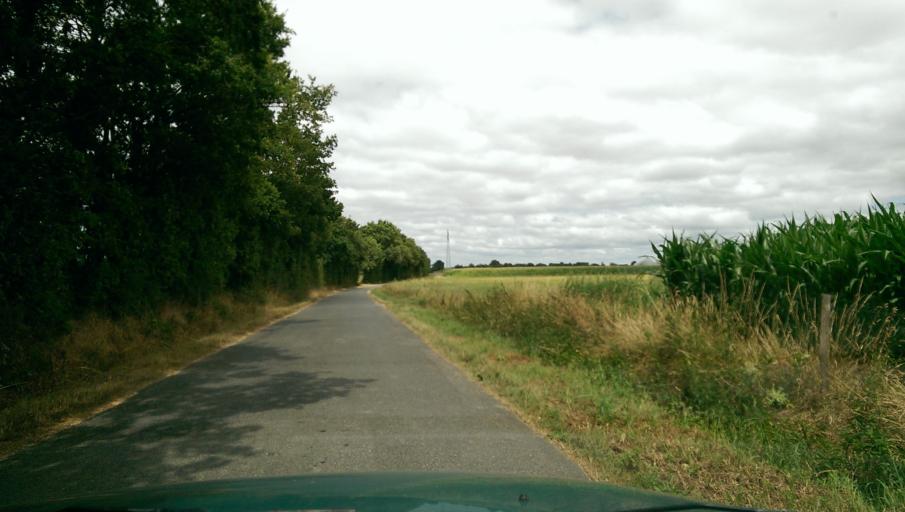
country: FR
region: Pays de la Loire
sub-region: Departement de la Loire-Atlantique
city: Vieillevigne
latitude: 46.9830
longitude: -1.4240
